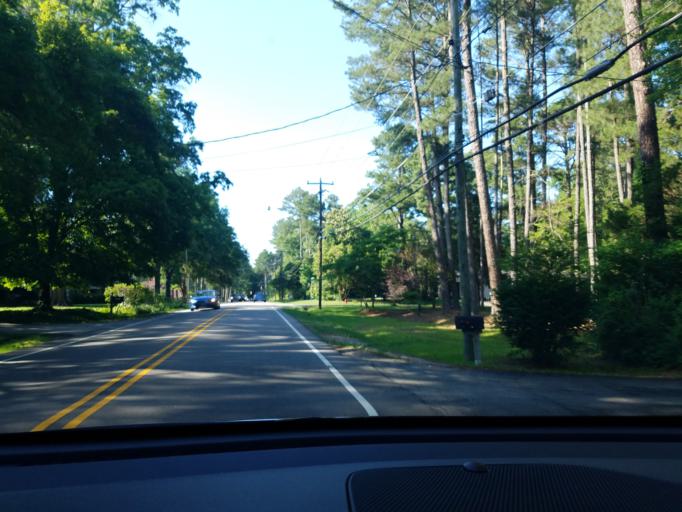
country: US
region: North Carolina
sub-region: Durham County
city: Durham
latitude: 35.9677
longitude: -78.9325
